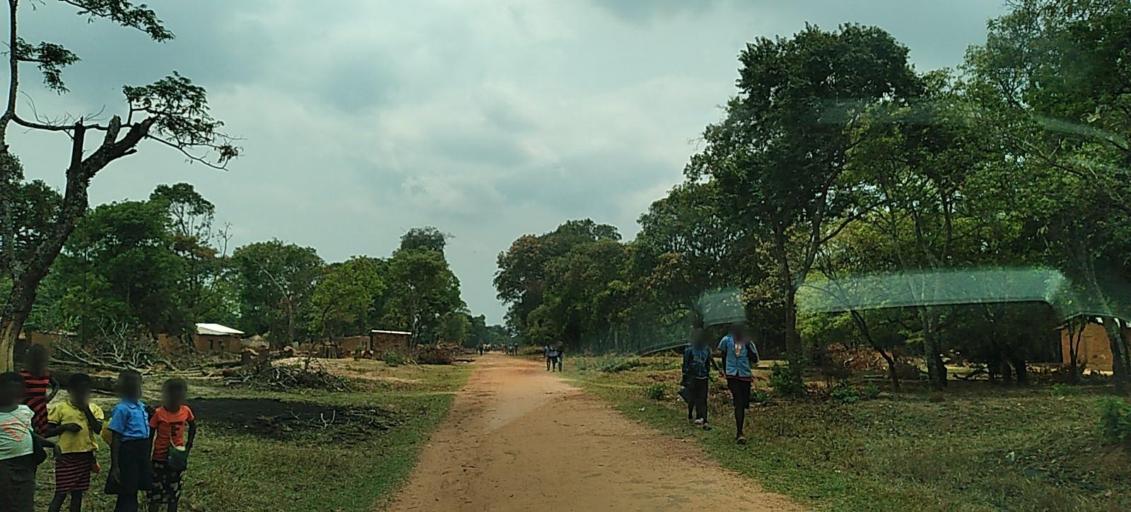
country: ZM
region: North-Western
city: Mwinilunga
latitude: -11.5261
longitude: 24.7866
